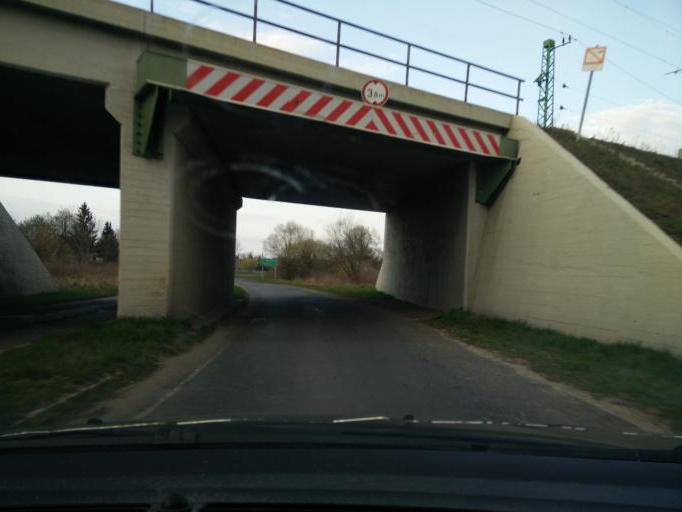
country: HU
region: Zala
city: Zalaszentgrot
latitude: 46.9821
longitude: 17.0331
